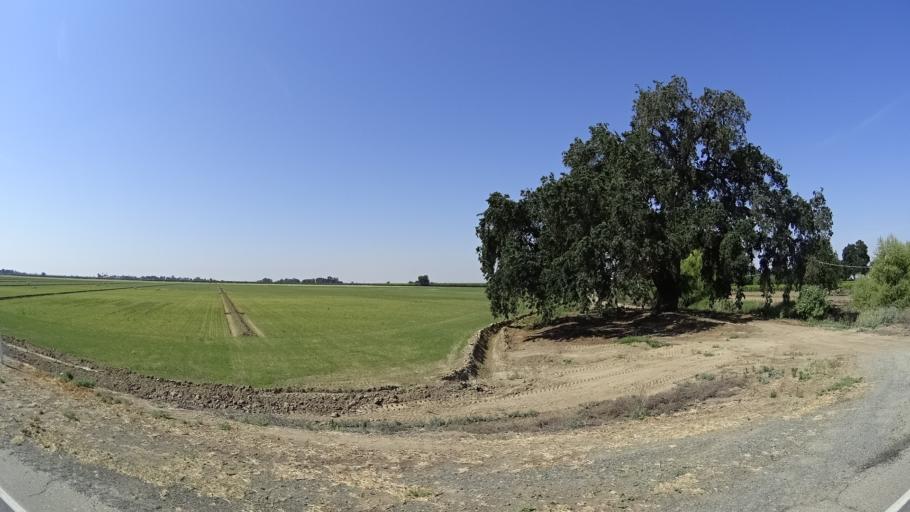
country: US
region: California
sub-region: Kings County
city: Lemoore
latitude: 36.3429
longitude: -119.8227
